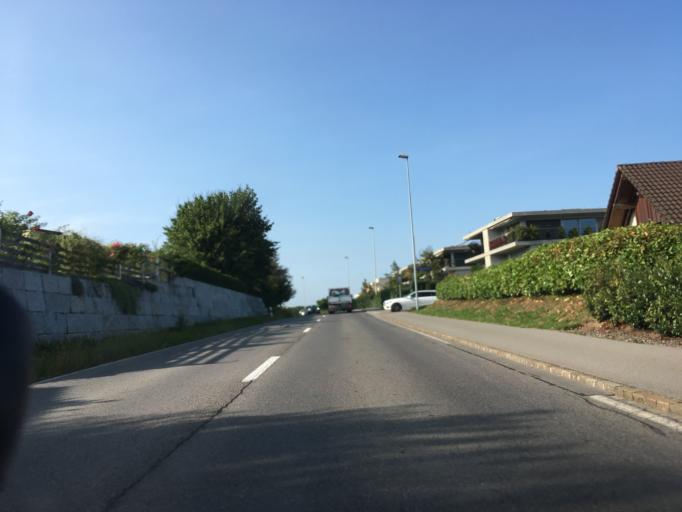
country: CH
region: Lucerne
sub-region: Lucerne-Land District
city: Meierskappel
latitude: 47.1425
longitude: 8.4528
